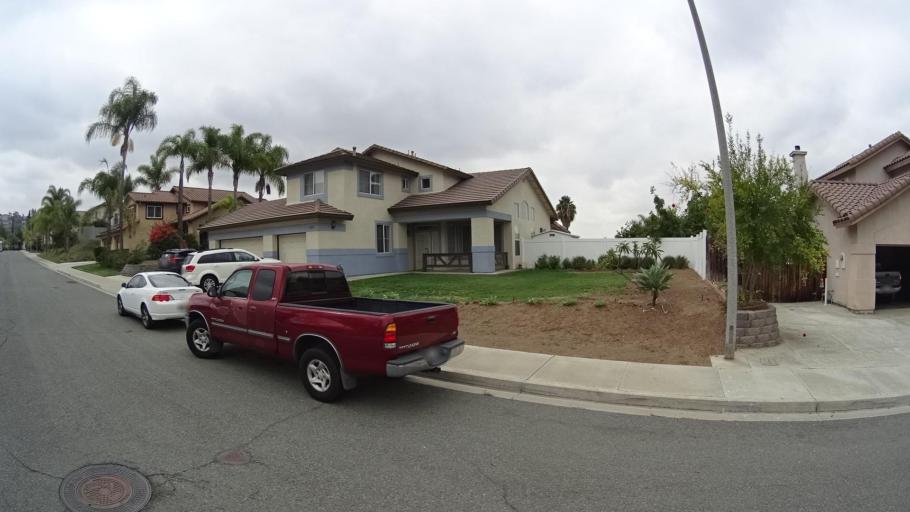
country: US
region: California
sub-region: San Diego County
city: Spring Valley
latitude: 32.7431
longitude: -116.9947
